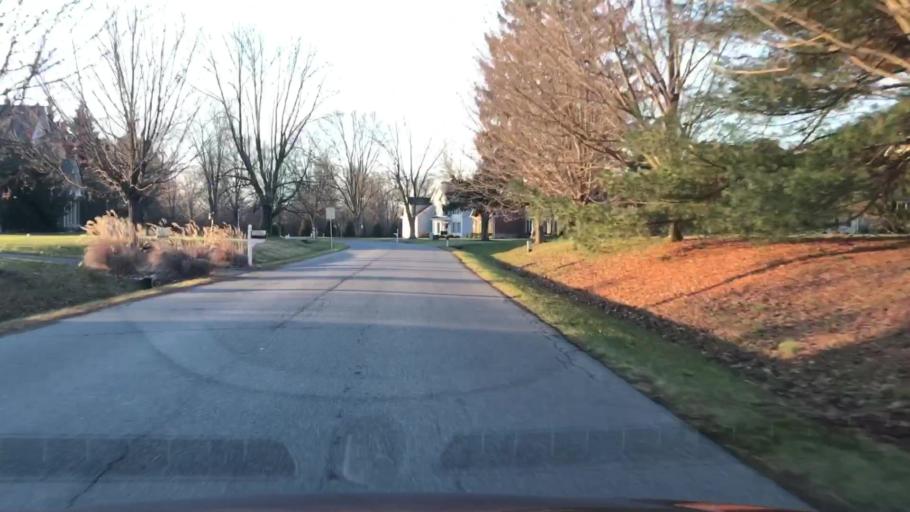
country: US
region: Maryland
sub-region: Howard County
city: Highland
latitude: 39.1785
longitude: -76.9387
